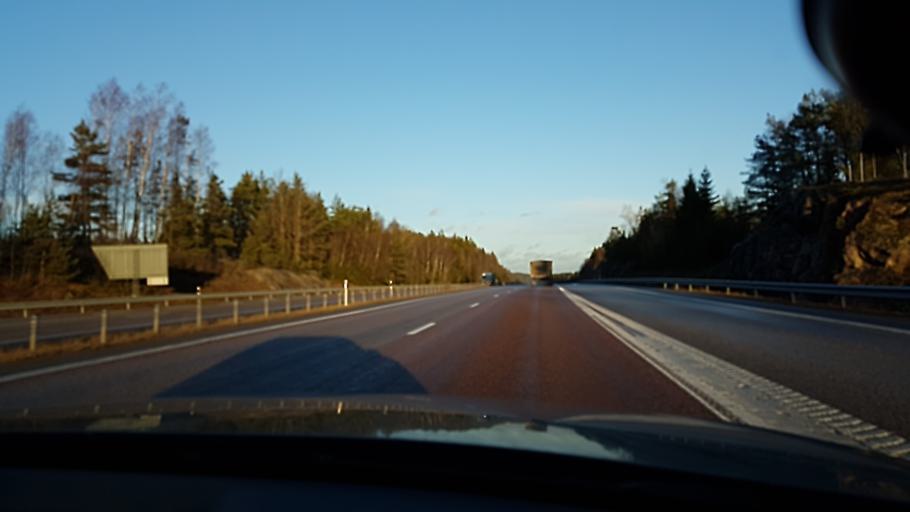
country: SE
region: Soedermanland
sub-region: Gnesta Kommun
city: Gnesta
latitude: 58.8591
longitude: 17.2124
